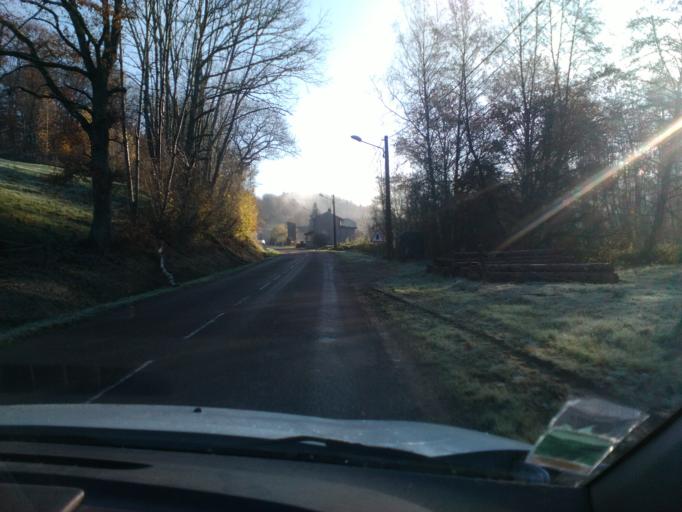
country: FR
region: Lorraine
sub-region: Departement des Vosges
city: Uzemain
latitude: 48.0641
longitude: 6.3275
